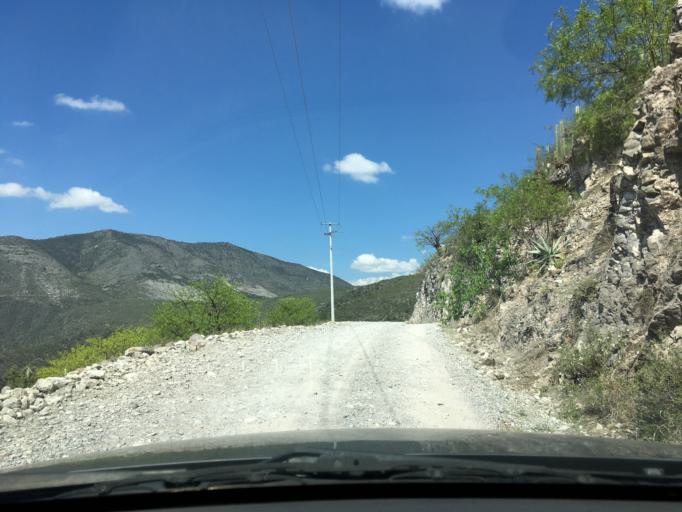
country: MX
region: Hidalgo
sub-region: Metztitlan
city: Fontezuelas
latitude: 20.6342
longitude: -98.8434
